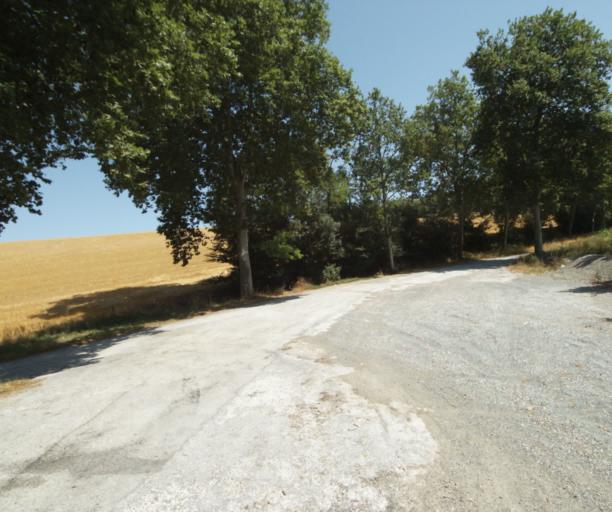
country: FR
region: Midi-Pyrenees
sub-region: Departement de la Haute-Garonne
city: Saint-Felix-Lauragais
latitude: 43.4615
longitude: 1.8582
